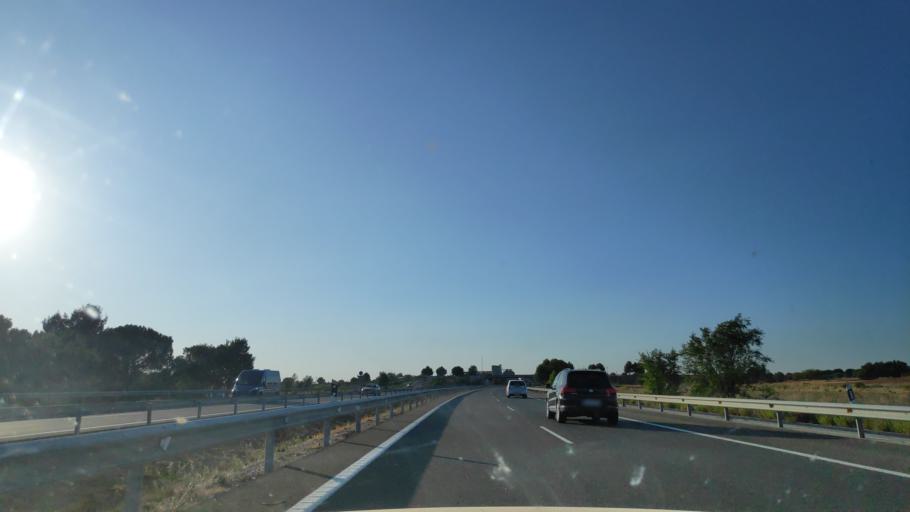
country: ES
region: Castille-La Mancha
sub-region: Provincia de Cuenca
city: Tarancon
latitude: 40.0016
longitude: -3.0242
